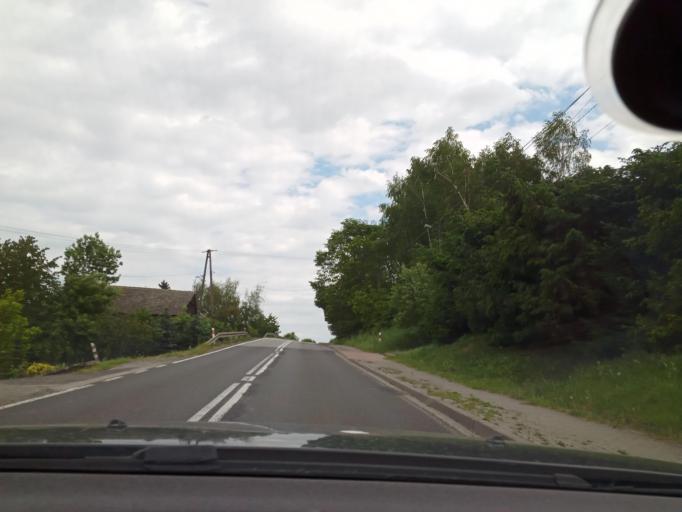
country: PL
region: Lesser Poland Voivodeship
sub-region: Powiat wielicki
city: Trabki
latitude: 49.9543
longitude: 20.1554
